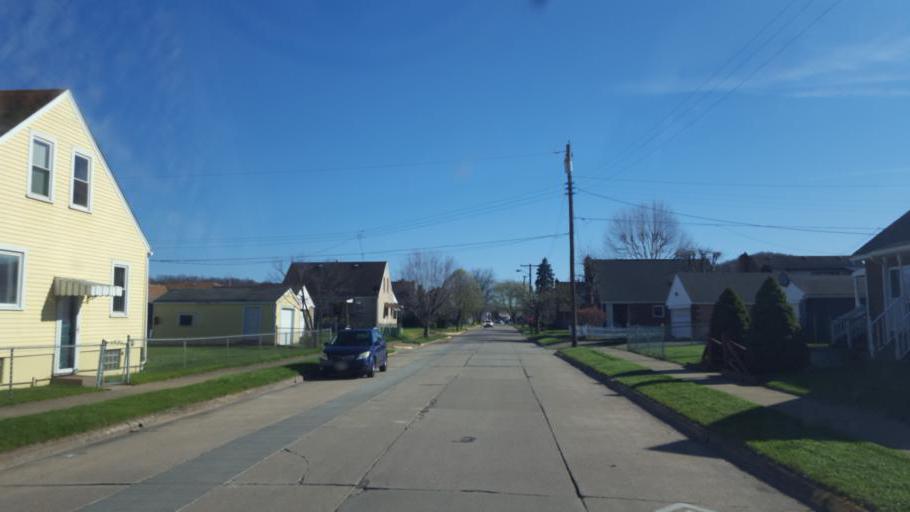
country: US
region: Ohio
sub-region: Jefferson County
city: Toronto
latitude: 40.4589
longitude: -80.6080
